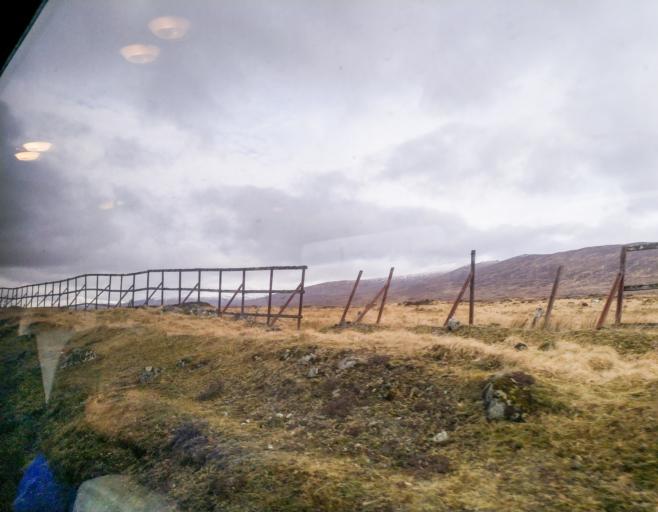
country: GB
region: Scotland
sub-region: Highland
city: Spean Bridge
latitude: 56.7041
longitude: -4.5884
